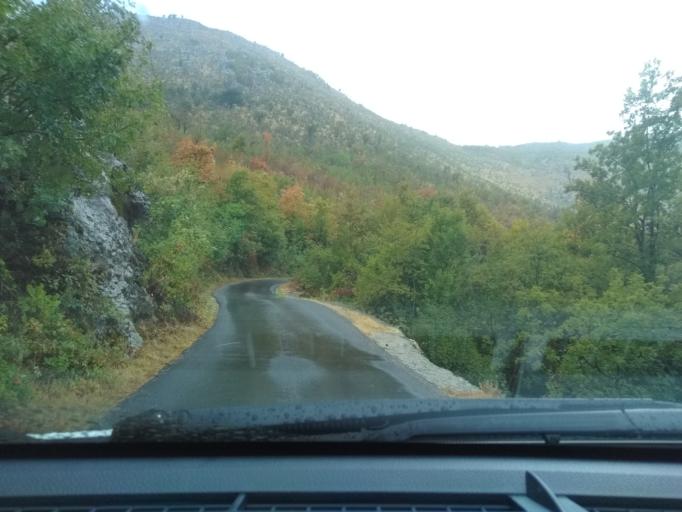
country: ME
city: Stari Bar
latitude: 42.1815
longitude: 19.1783
